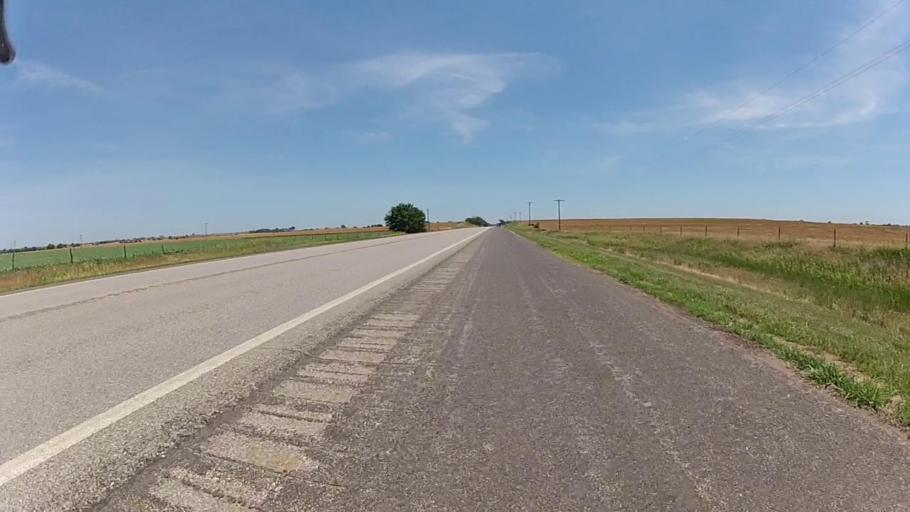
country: US
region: Kansas
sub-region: Barber County
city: Medicine Lodge
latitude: 37.2537
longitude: -98.3922
